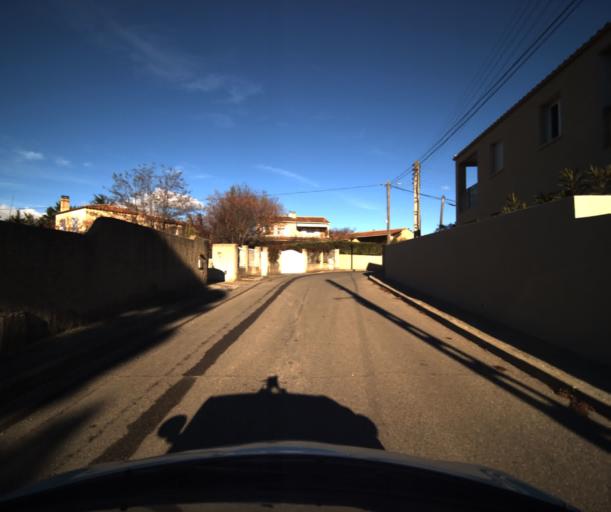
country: FR
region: Provence-Alpes-Cote d'Azur
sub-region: Departement du Vaucluse
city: Pertuis
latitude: 43.7032
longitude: 5.5040
